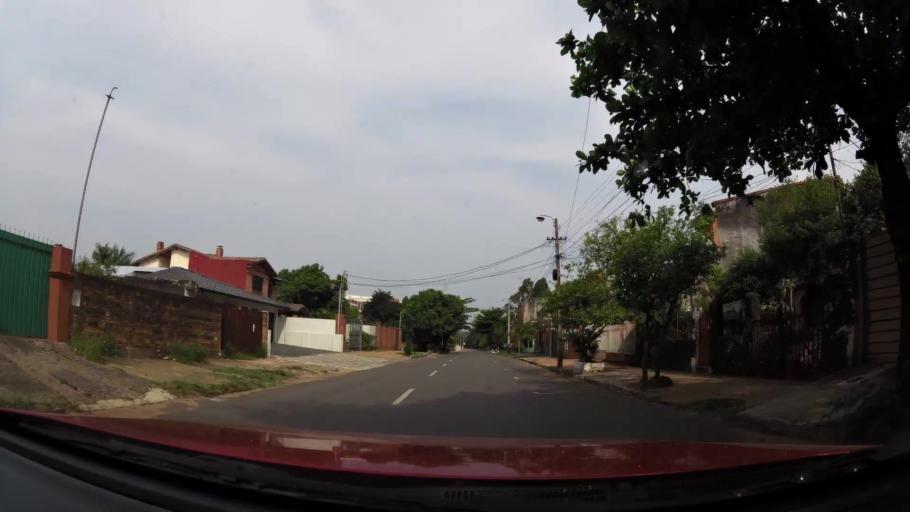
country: PY
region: Central
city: Fernando de la Mora
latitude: -25.3026
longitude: -57.5578
